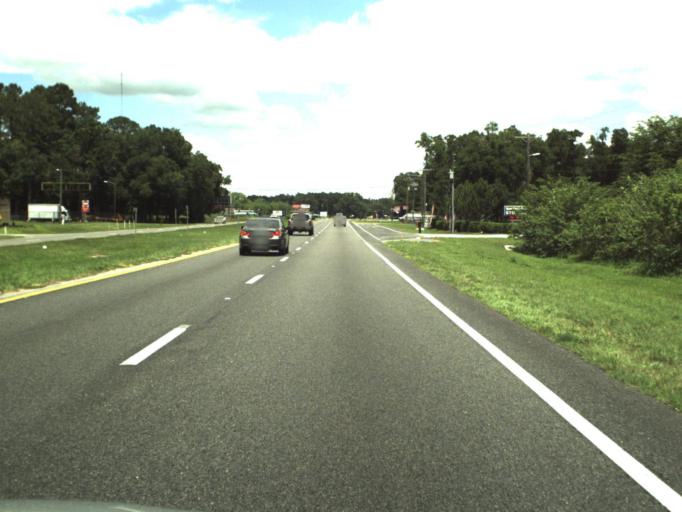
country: US
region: Florida
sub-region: Marion County
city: Ocala
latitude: 29.2321
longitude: -82.1501
